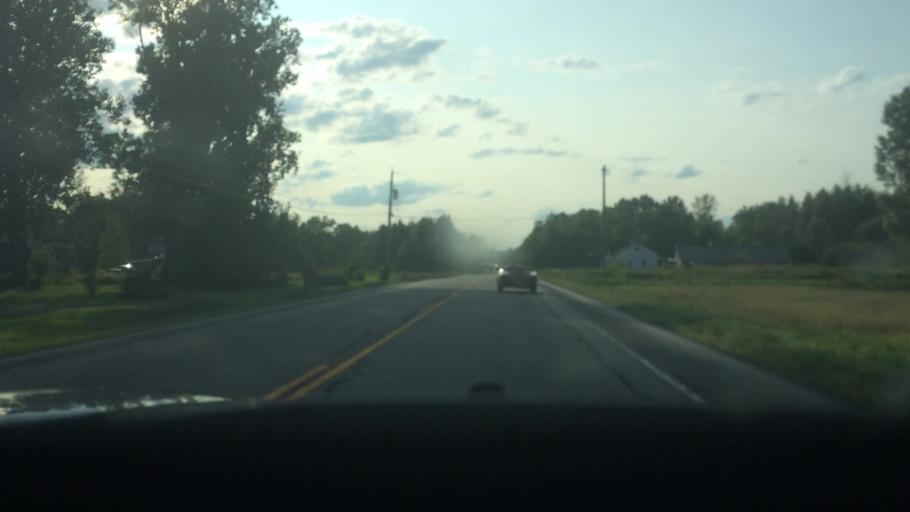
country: US
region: New York
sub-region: St. Lawrence County
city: Canton
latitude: 44.6553
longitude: -75.3146
